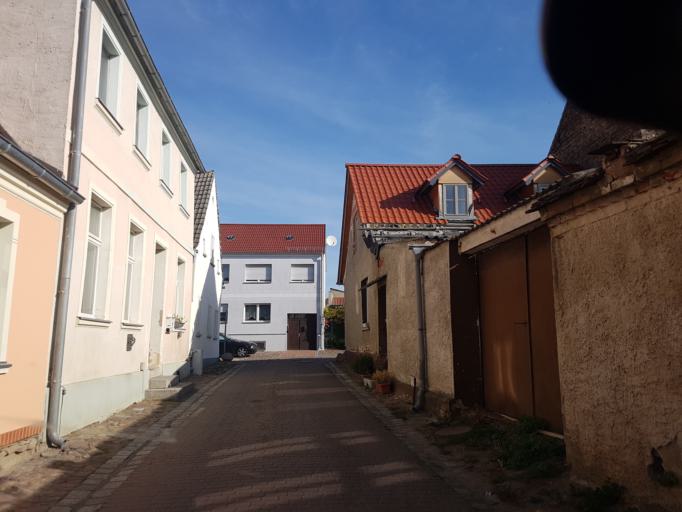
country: DE
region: Brandenburg
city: Niemegk
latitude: 52.0740
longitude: 12.6874
